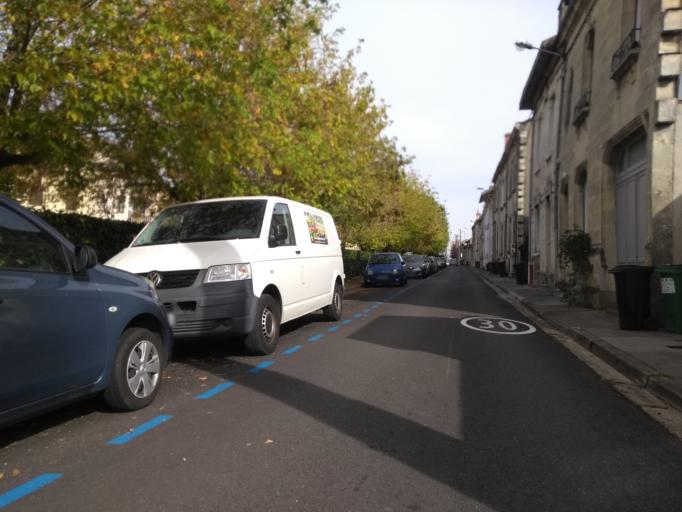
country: FR
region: Aquitaine
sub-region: Departement de la Gironde
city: Talence
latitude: 44.8210
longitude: -0.5918
